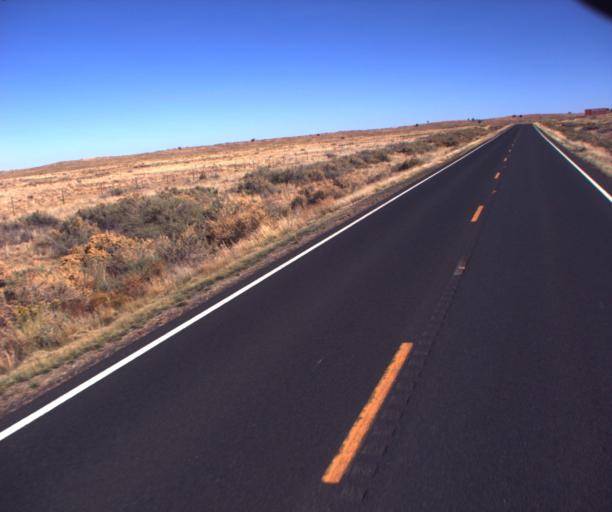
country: US
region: Arizona
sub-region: Apache County
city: Ganado
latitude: 35.7875
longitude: -109.6866
